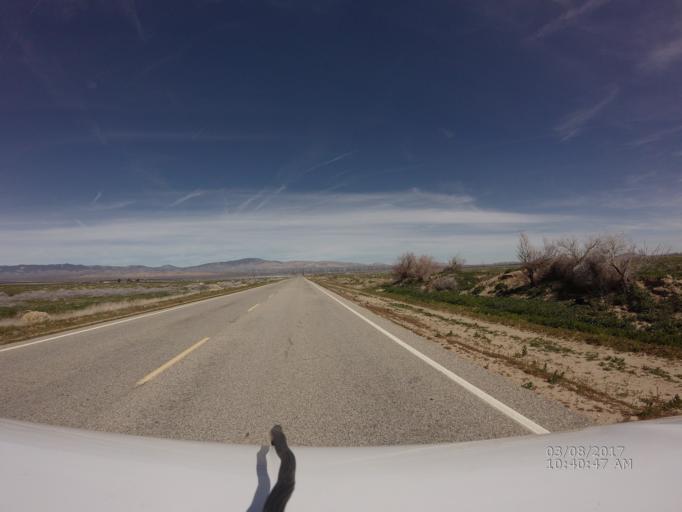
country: US
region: California
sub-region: Los Angeles County
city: Green Valley
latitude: 34.8063
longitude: -118.4315
